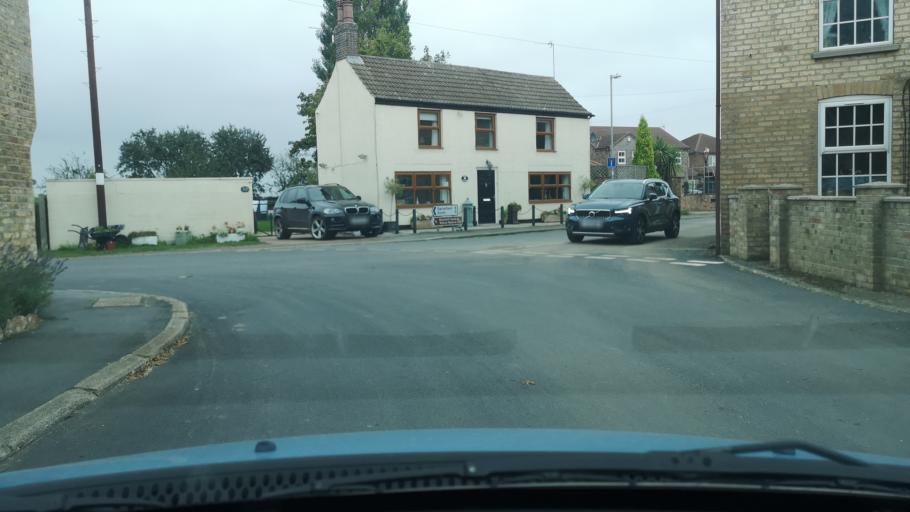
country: GB
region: England
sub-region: North Lincolnshire
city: Burton upon Stather
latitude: 53.6790
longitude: -0.7230
